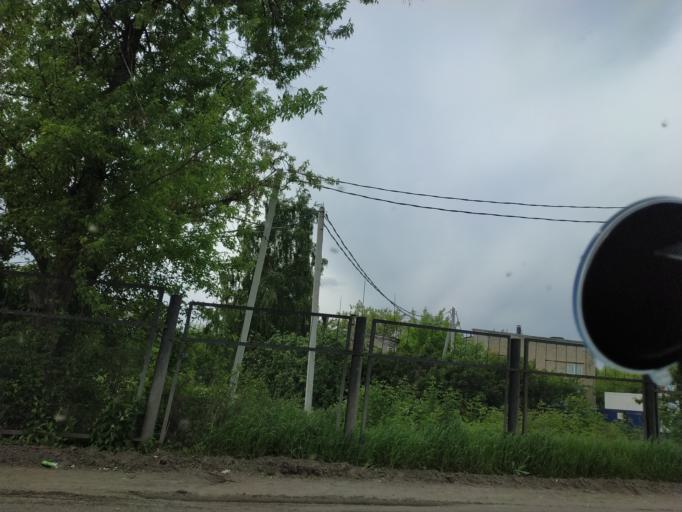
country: RU
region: Moskovskaya
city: Zhukovskiy
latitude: 55.5697
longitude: 38.1148
